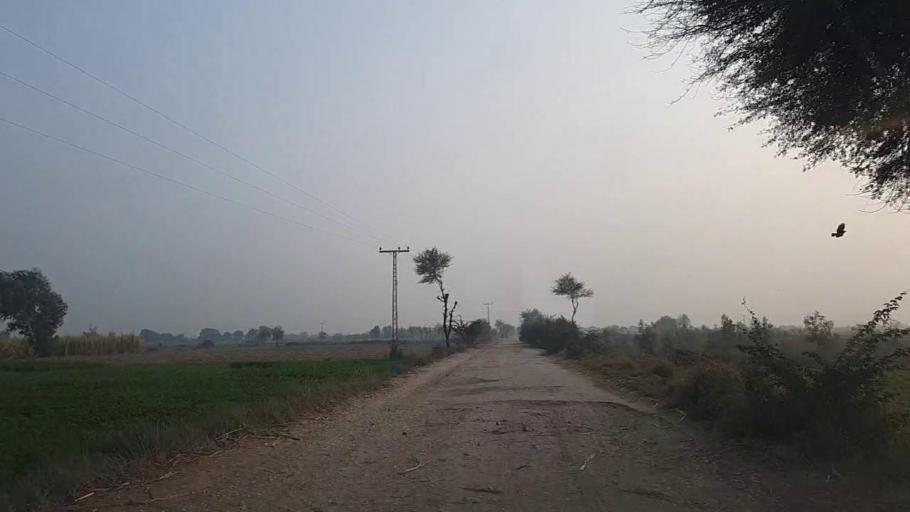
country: PK
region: Sindh
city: Sinjhoro
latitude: 26.1116
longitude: 68.7964
